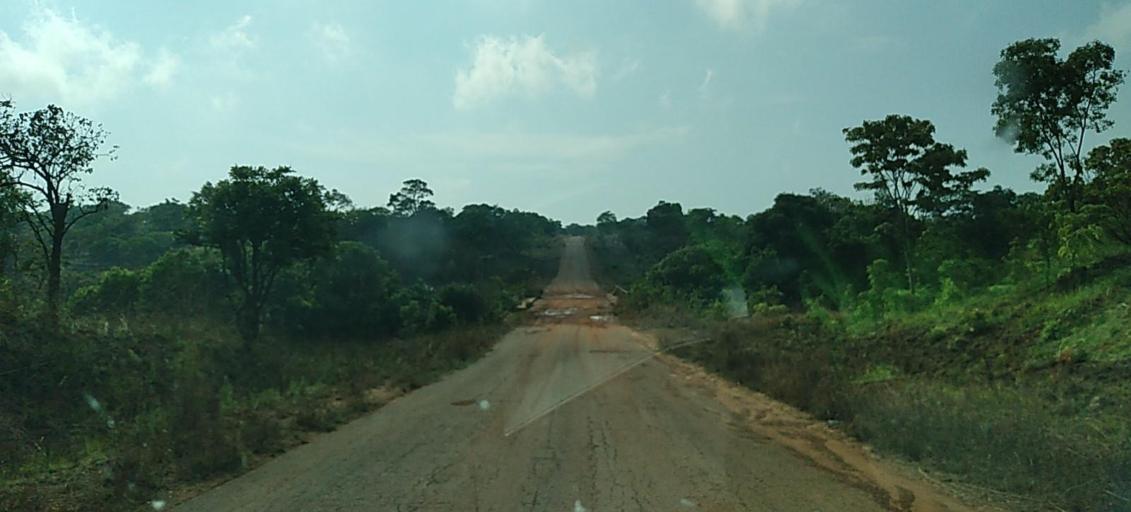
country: ZM
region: North-Western
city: Mwinilunga
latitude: -11.7698
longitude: 25.0080
